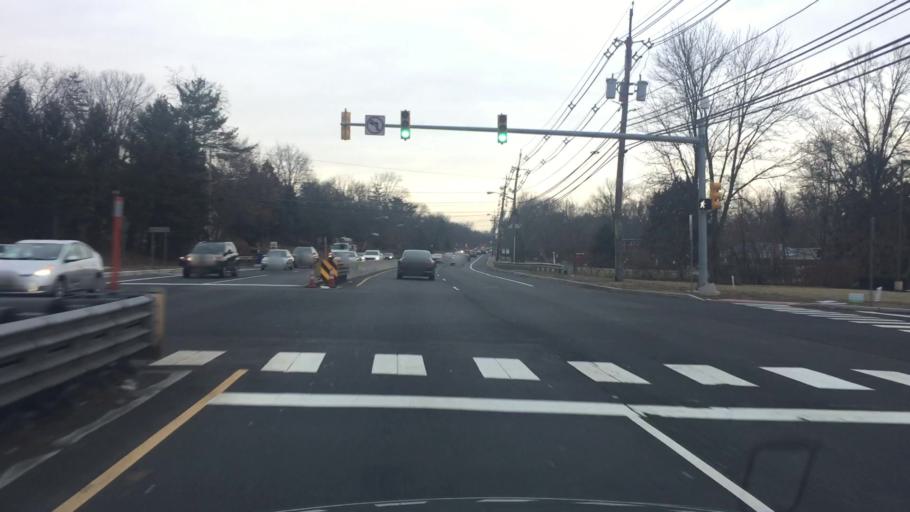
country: US
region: New Jersey
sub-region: Somerset County
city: Somerset
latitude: 40.5176
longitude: -74.4906
